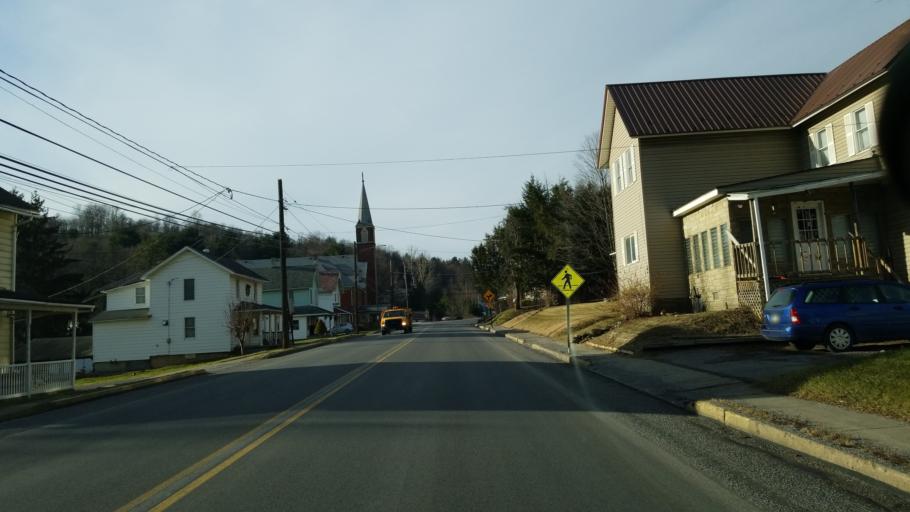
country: US
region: Pennsylvania
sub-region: Clearfield County
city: Curwensville
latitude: 40.9662
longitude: -78.6147
